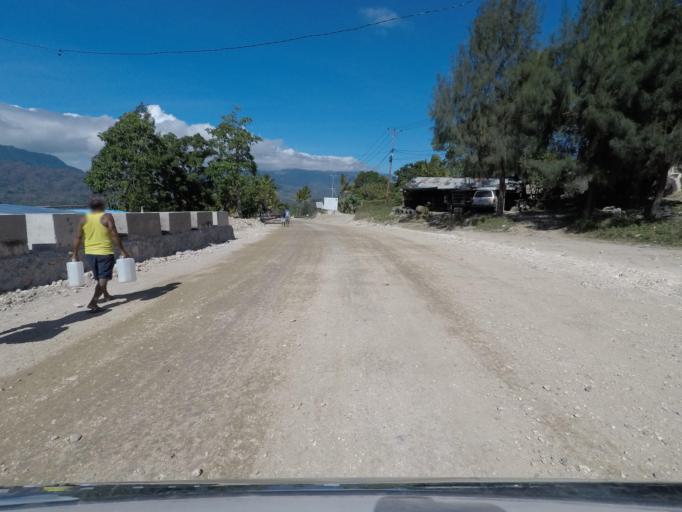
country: TL
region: Baucau
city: Venilale
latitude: -8.6443
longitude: 126.3757
